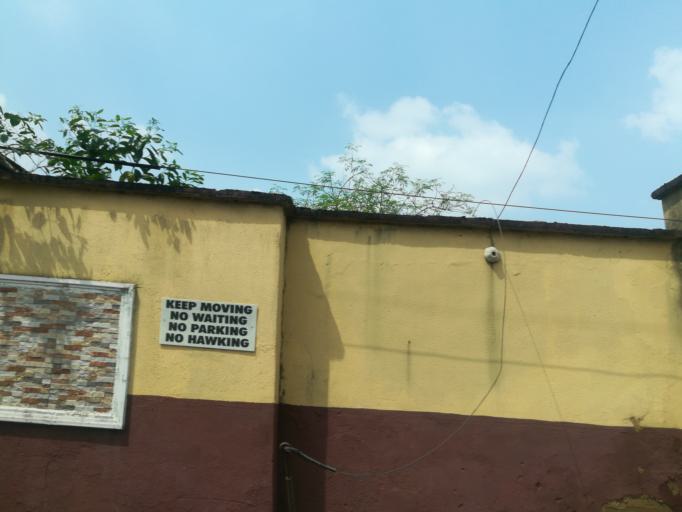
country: NG
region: Oyo
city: Ibadan
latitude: 7.3970
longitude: 3.9172
